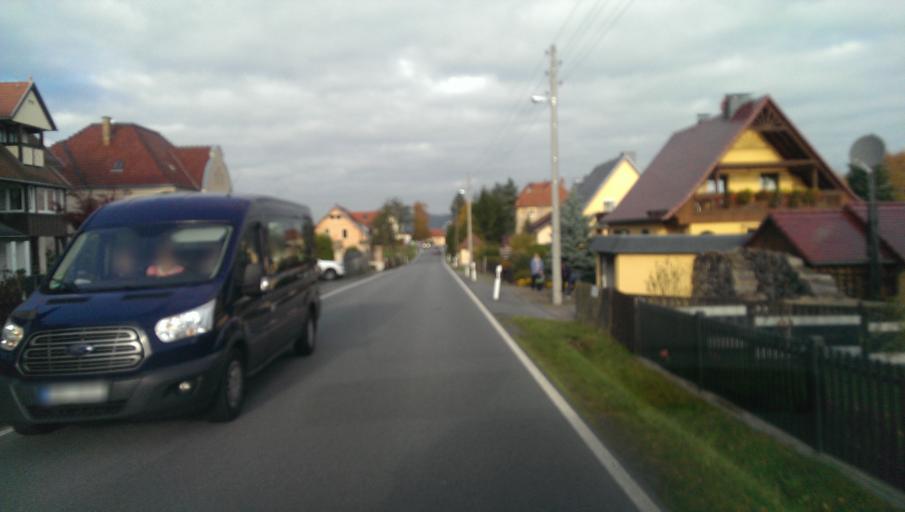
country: DE
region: Saxony
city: Porschdorf
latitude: 50.9504
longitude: 14.1103
